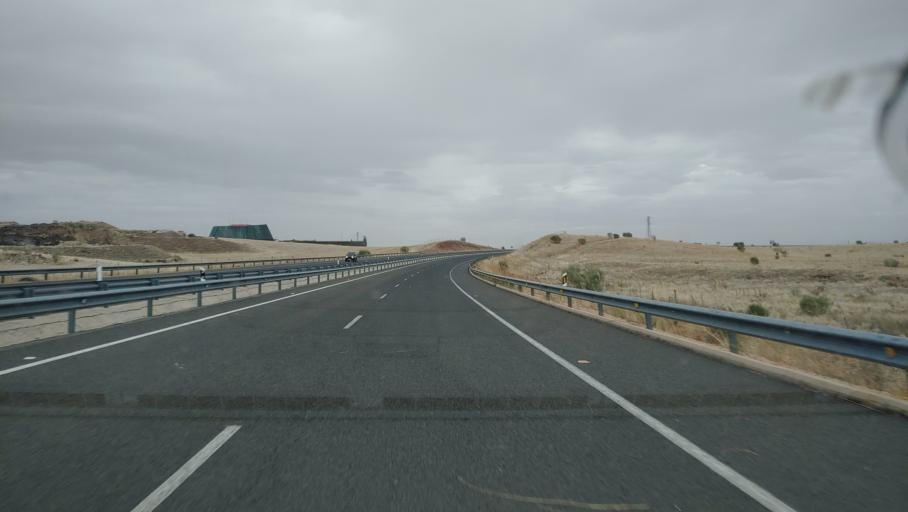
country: ES
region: Castille-La Mancha
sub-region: Provincia de Ciudad Real
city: Canada de Calatrava
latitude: 38.8740
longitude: -3.9993
